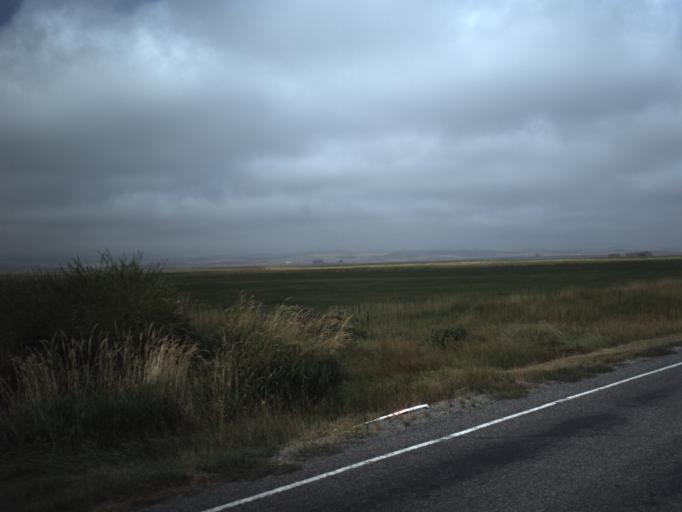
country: US
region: Utah
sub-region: Rich County
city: Randolph
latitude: 41.4702
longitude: -111.1069
